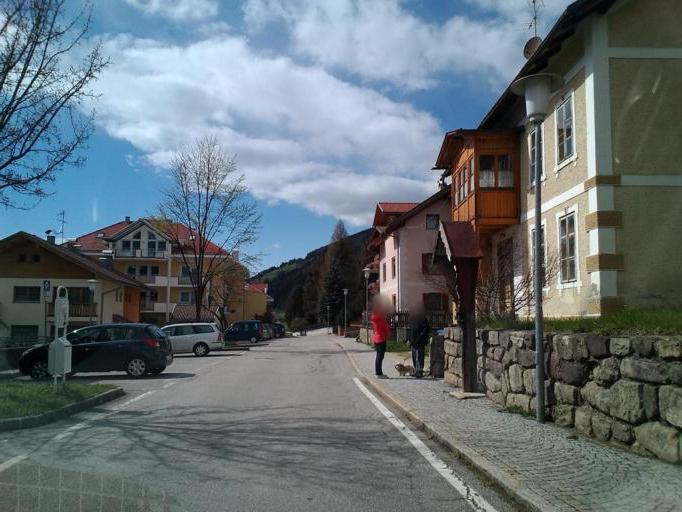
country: IT
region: Trentino-Alto Adige
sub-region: Bolzano
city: Villabassa
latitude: 46.7398
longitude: 12.1685
